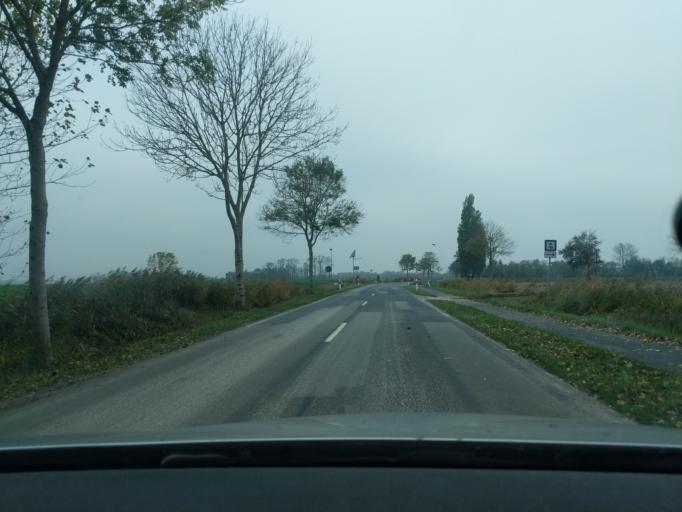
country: DE
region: Lower Saxony
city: Otterndorf
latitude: 53.8182
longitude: 8.8651
